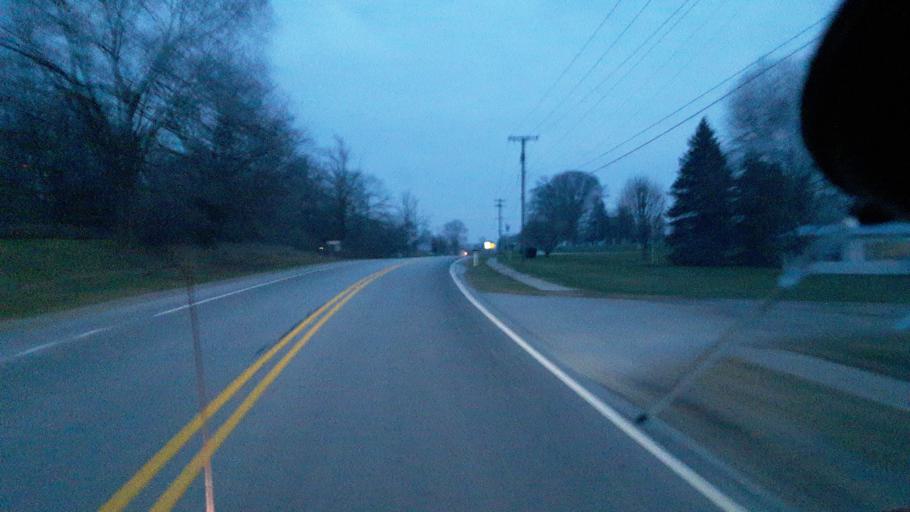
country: US
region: Indiana
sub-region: LaGrange County
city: Lagrange
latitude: 41.6325
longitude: -85.4164
